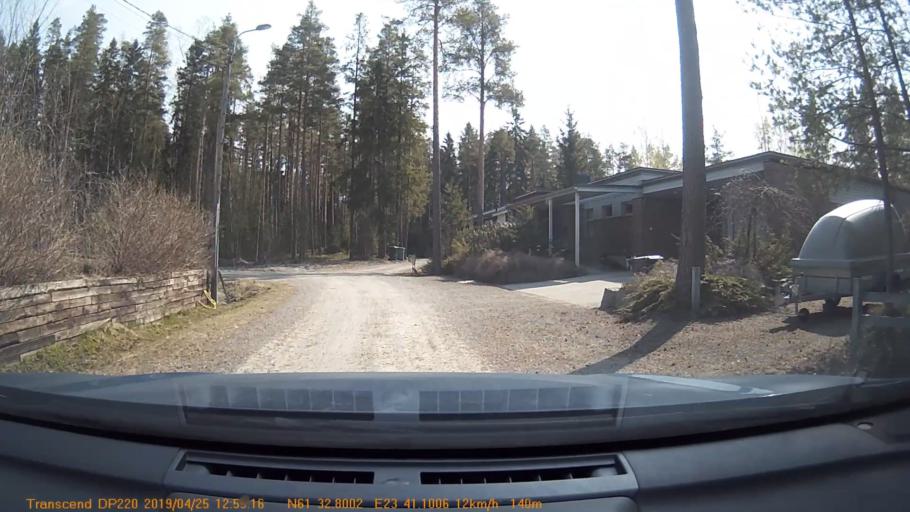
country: FI
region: Pirkanmaa
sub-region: Tampere
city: Yloejaervi
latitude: 61.5467
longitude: 23.6851
